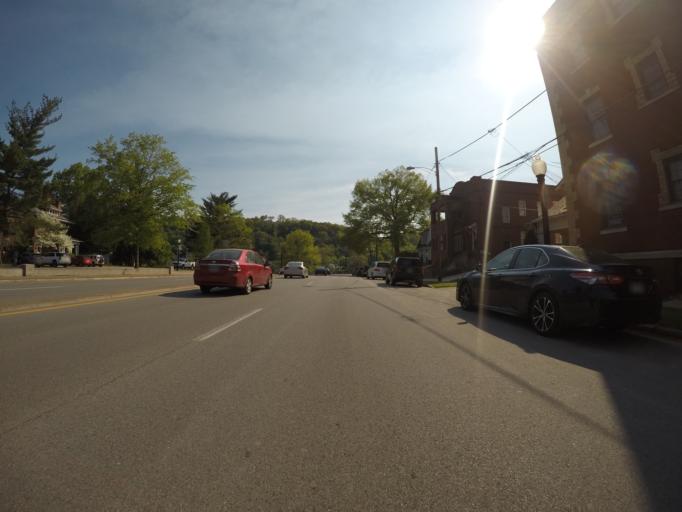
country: US
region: West Virginia
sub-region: Kanawha County
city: Charleston
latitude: 38.3371
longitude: -81.6159
